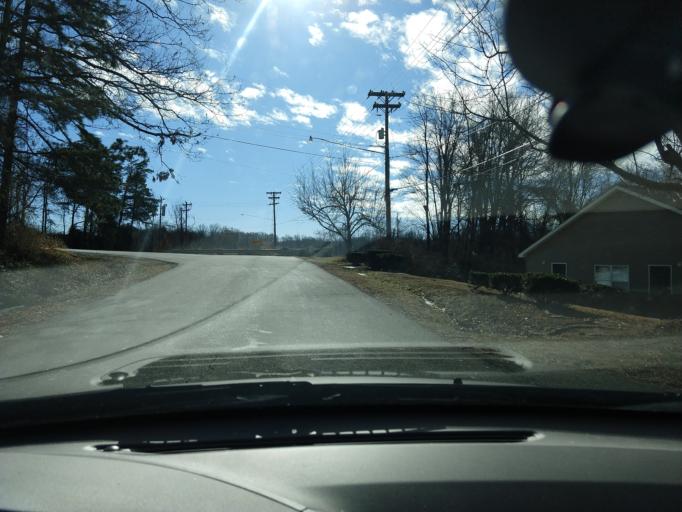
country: US
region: North Carolina
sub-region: Guilford County
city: Greensboro
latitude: 36.0535
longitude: -79.8663
